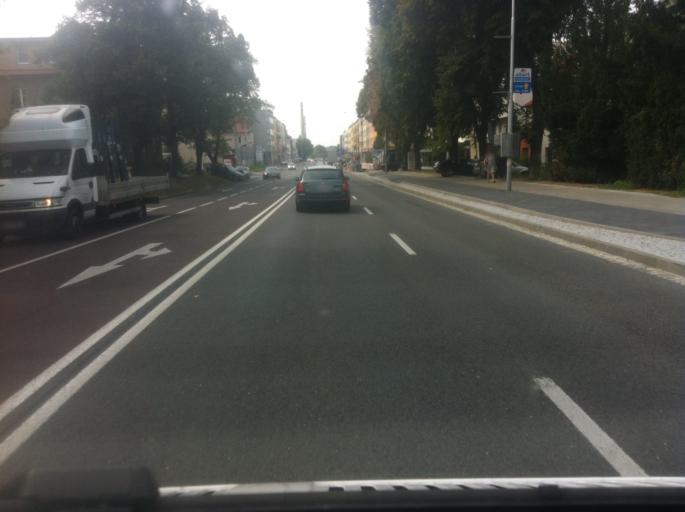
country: CZ
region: Zlin
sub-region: Okres Zlin
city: Zlin
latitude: 49.2256
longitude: 17.6749
